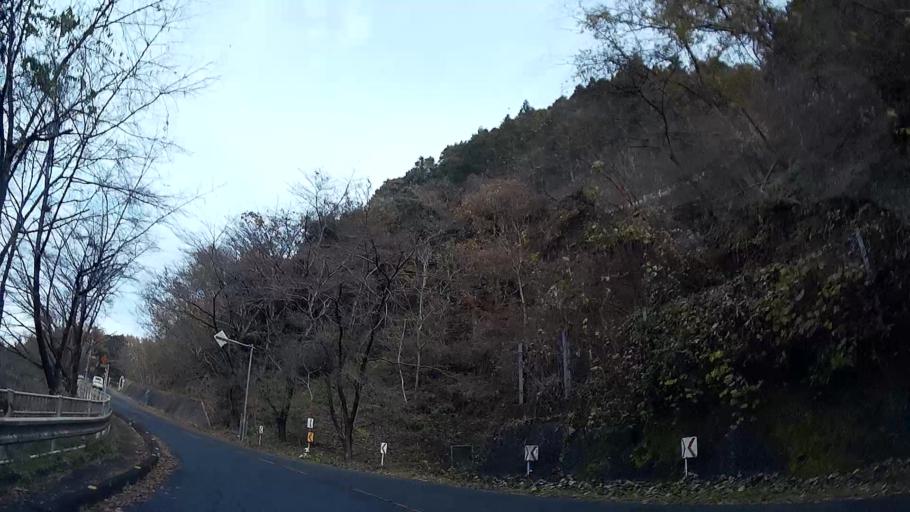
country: JP
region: Saitama
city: Chichibu
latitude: 35.9567
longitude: 139.0553
